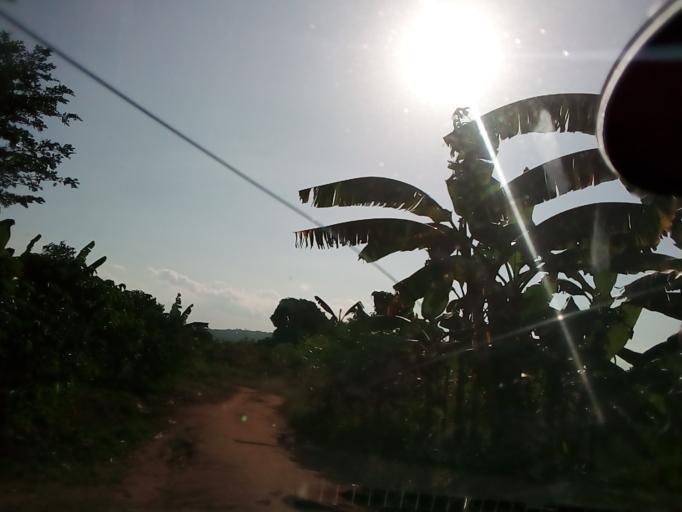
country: UG
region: Central Region
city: Masaka
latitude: -0.2700
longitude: 31.7207
